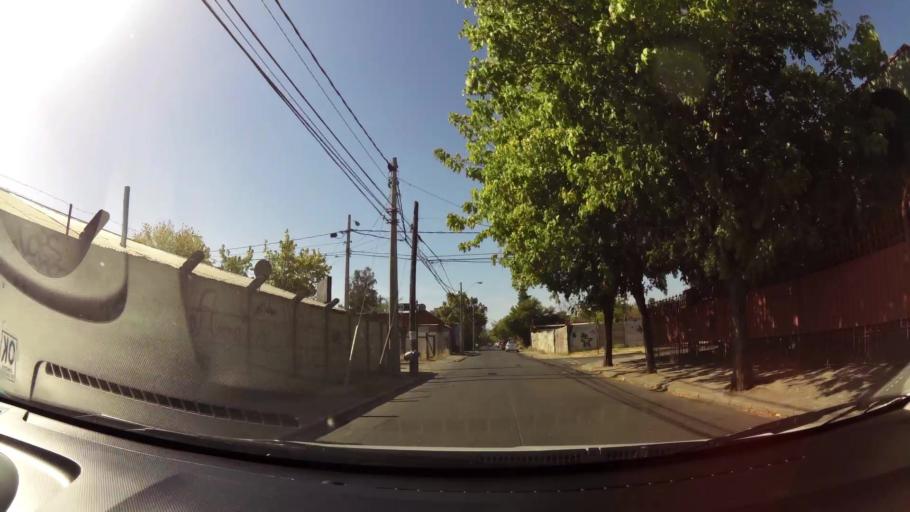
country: CL
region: Maule
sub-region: Provincia de Talca
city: Talca
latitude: -35.4317
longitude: -71.6672
